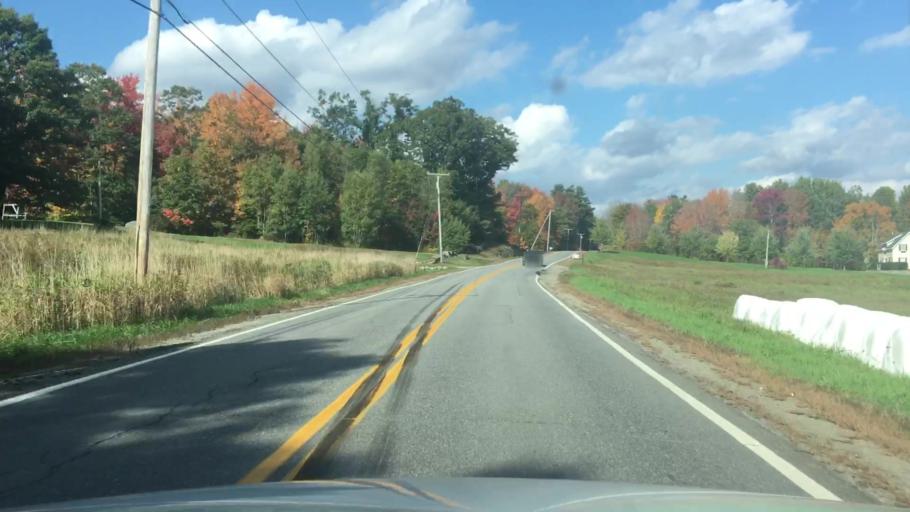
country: US
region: Maine
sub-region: Knox County
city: Union
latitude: 44.2511
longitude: -69.2781
